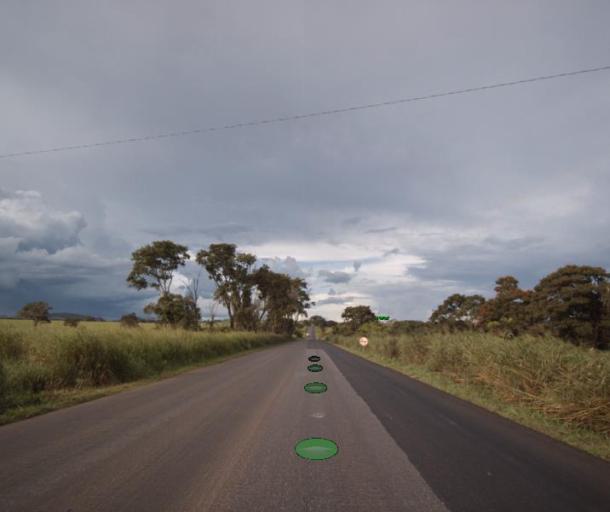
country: BR
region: Goias
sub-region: Itapaci
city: Itapaci
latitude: -15.1367
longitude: -49.5209
